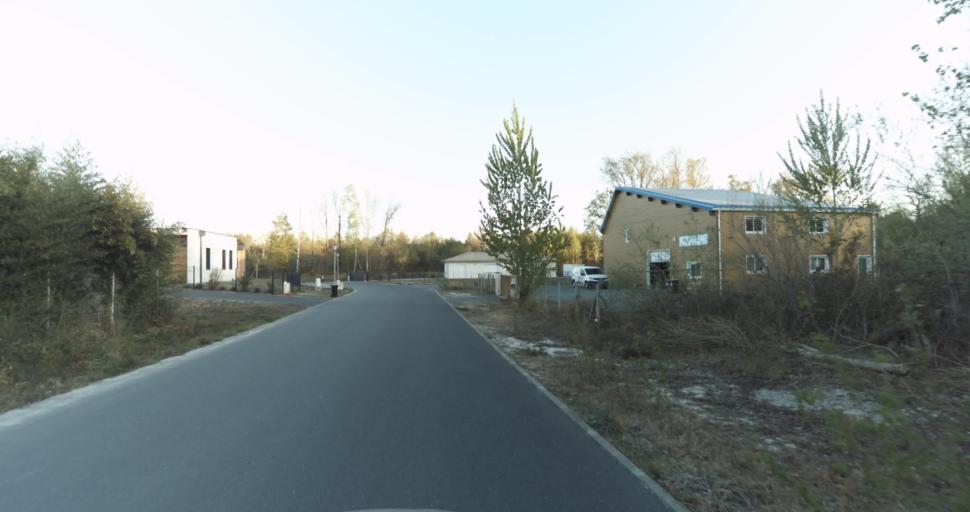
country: FR
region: Aquitaine
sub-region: Departement de la Gironde
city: Martignas-sur-Jalle
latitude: 44.8102
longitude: -0.7676
